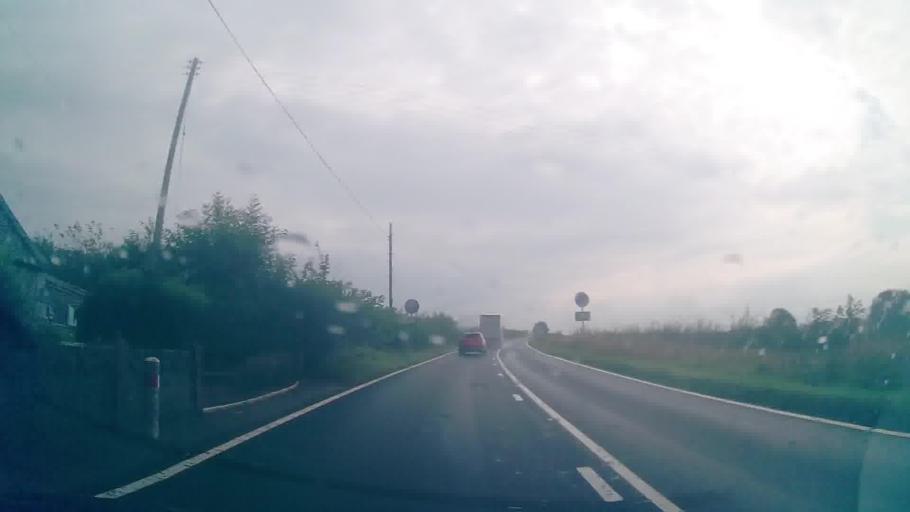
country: GB
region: Scotland
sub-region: Dumfries and Galloway
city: Lochmaben
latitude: 55.0590
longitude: -3.4759
